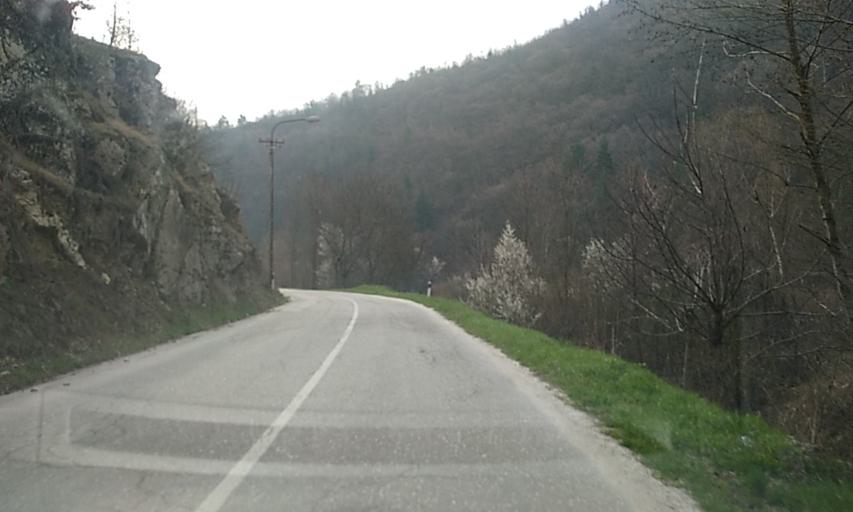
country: RS
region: Central Serbia
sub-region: Pcinjski Okrug
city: Bosilegrad
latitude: 42.4975
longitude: 22.4616
